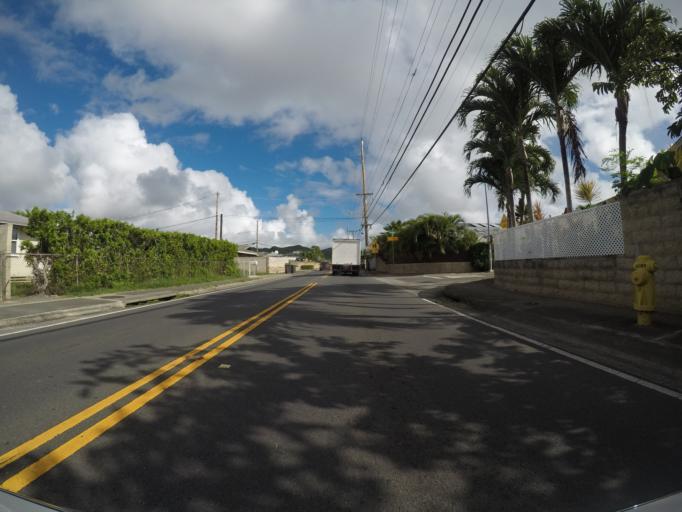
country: US
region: Hawaii
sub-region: Honolulu County
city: Kailua
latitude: 21.3992
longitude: -157.7474
